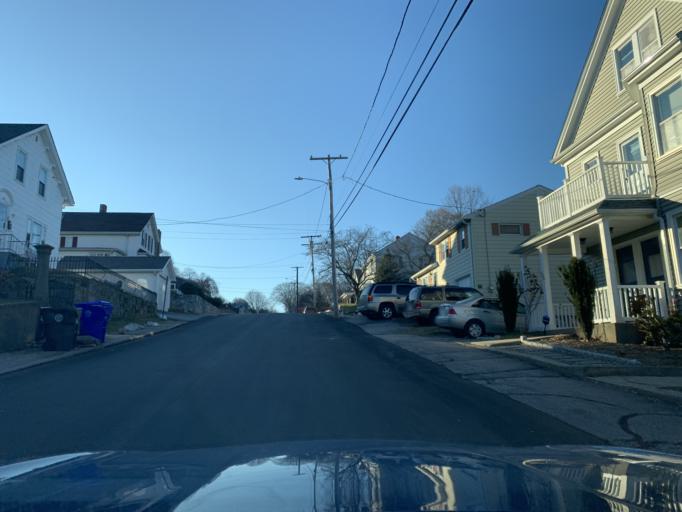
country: US
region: Rhode Island
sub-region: Kent County
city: West Warwick
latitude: 41.7123
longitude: -71.5262
